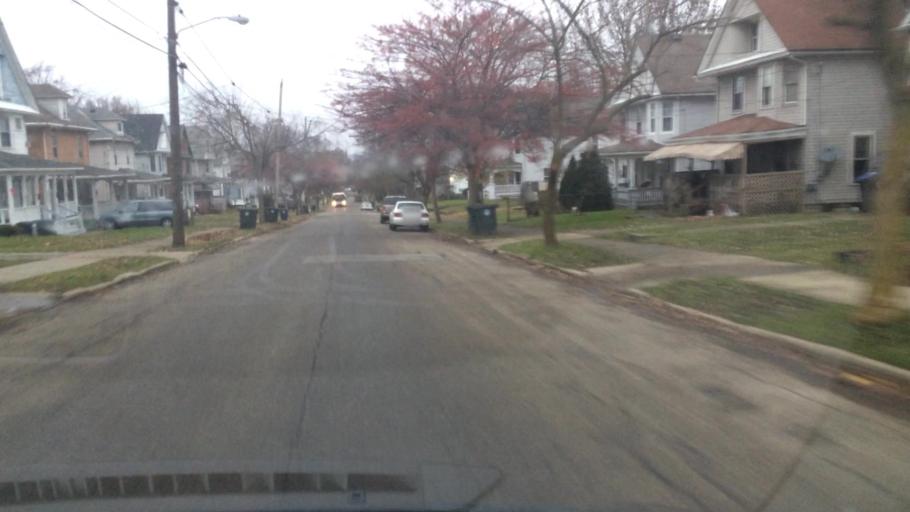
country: US
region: Ohio
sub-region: Summit County
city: Akron
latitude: 41.0632
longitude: -81.5343
